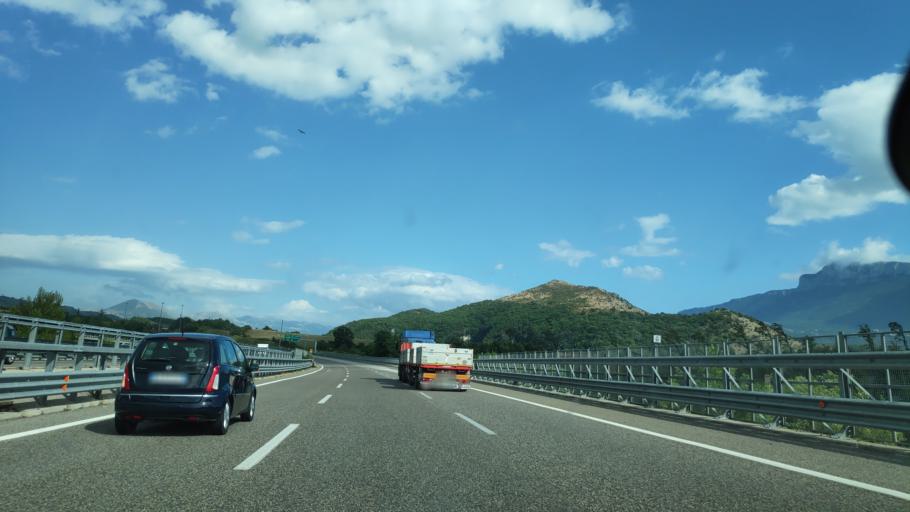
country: IT
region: Campania
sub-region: Provincia di Salerno
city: Palomonte
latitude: 40.6117
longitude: 15.2836
